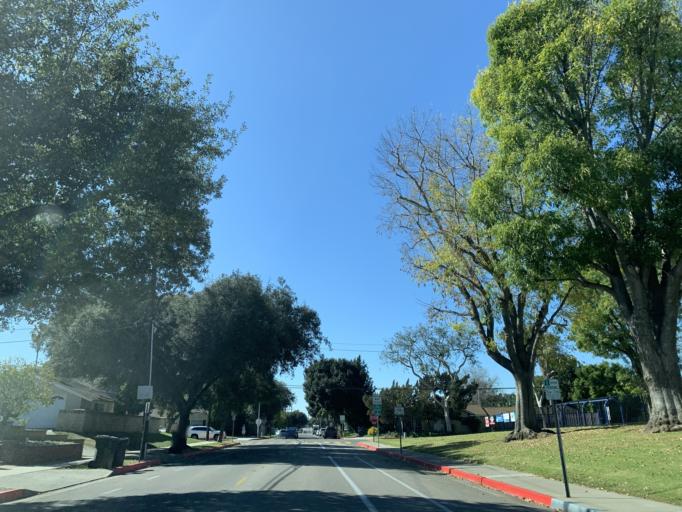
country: US
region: California
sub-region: Orange County
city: Placentia
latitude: 33.8814
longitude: -117.8977
